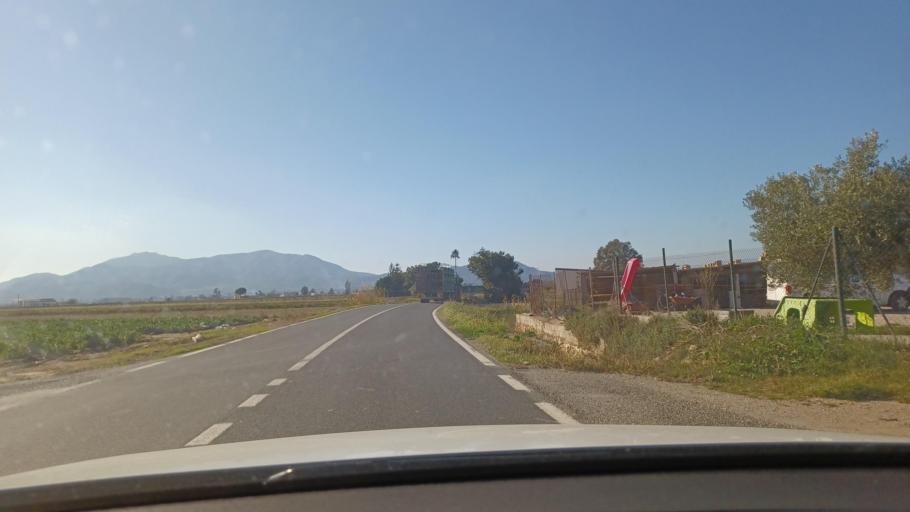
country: ES
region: Catalonia
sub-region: Provincia de Tarragona
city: Amposta
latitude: 40.7039
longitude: 0.6176
